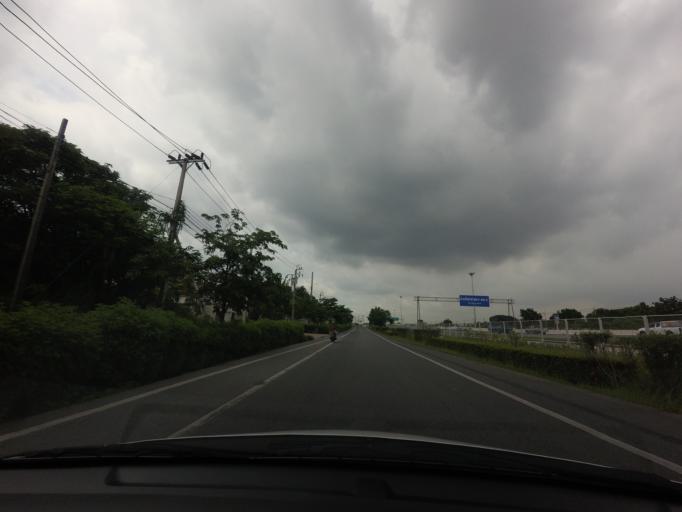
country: TH
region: Bangkok
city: Saphan Sung
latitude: 13.7690
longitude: 100.6916
